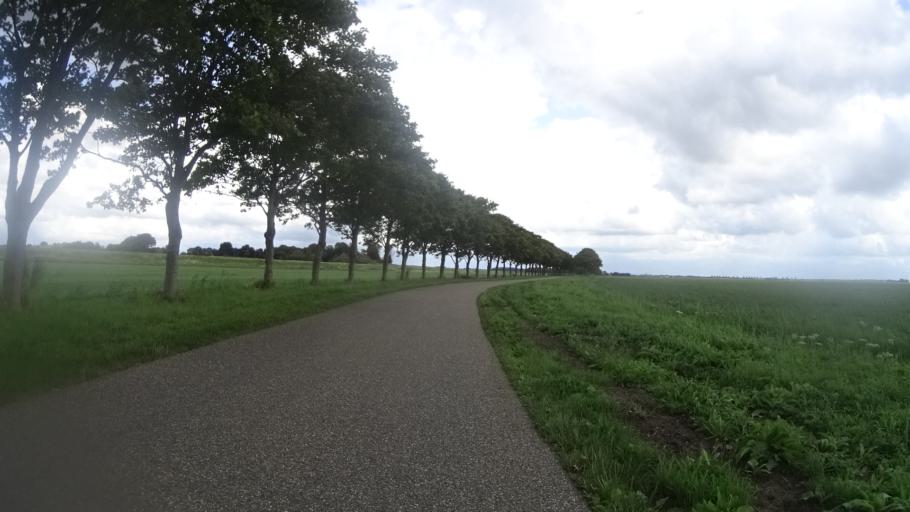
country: NL
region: North Holland
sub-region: Gemeente Hollands Kroon
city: Den Oever
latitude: 52.8891
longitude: 4.9432
